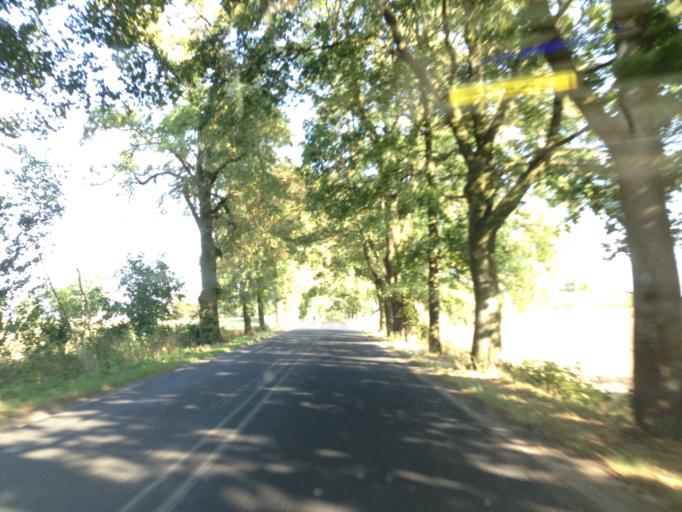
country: PL
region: Kujawsko-Pomorskie
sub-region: Powiat grudziadzki
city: Lasin
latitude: 53.5151
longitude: 19.1570
